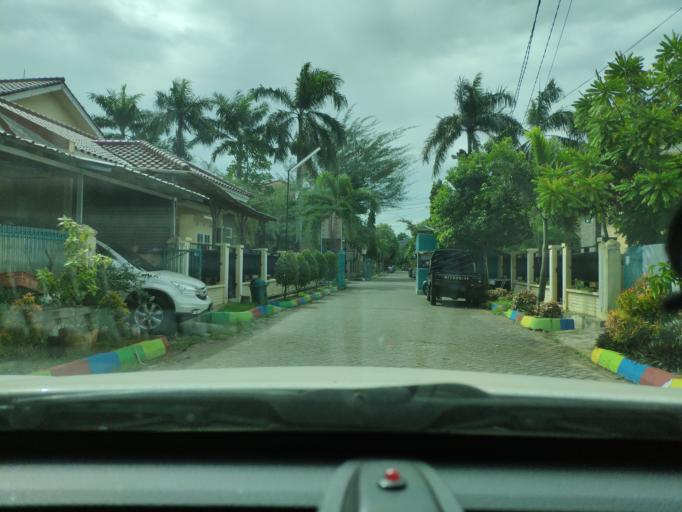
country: ID
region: West Java
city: Ciputat
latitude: -6.2208
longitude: 106.7085
